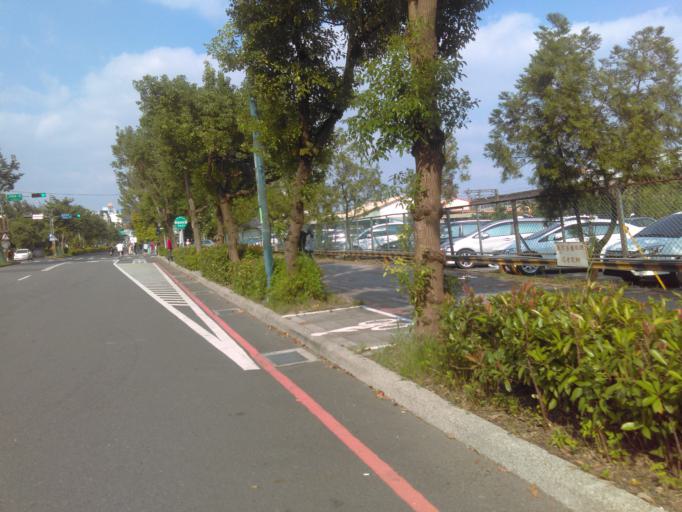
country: TW
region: Taiwan
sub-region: Yilan
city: Yilan
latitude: 24.7515
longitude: 121.7564
